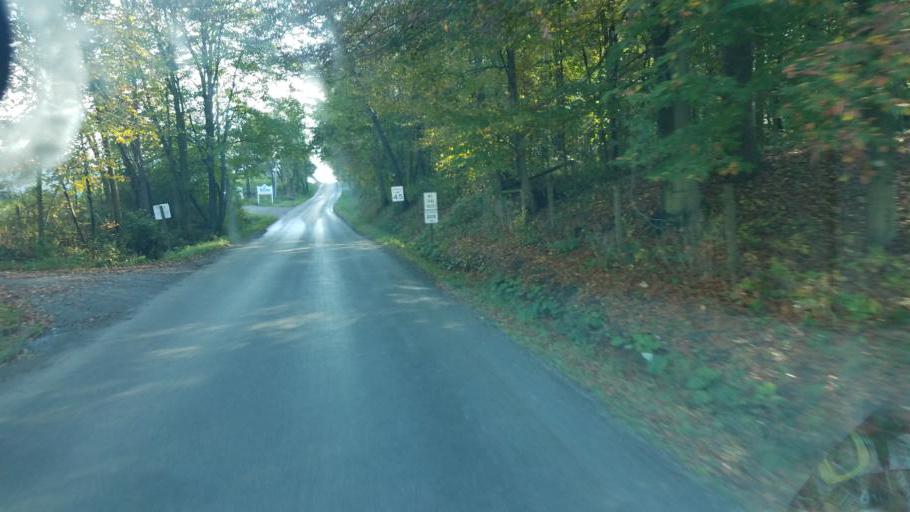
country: US
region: Ohio
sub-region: Wayne County
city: Apple Creek
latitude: 40.6678
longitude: -81.8420
